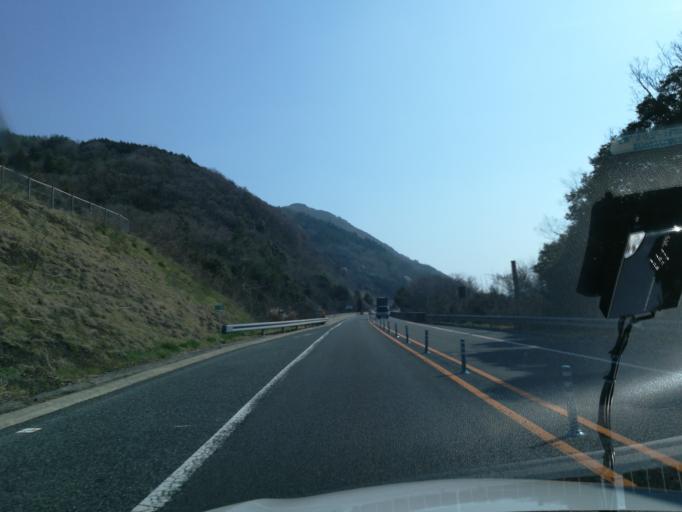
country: JP
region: Tokushima
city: Ikedacho
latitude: 34.0099
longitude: 133.7268
